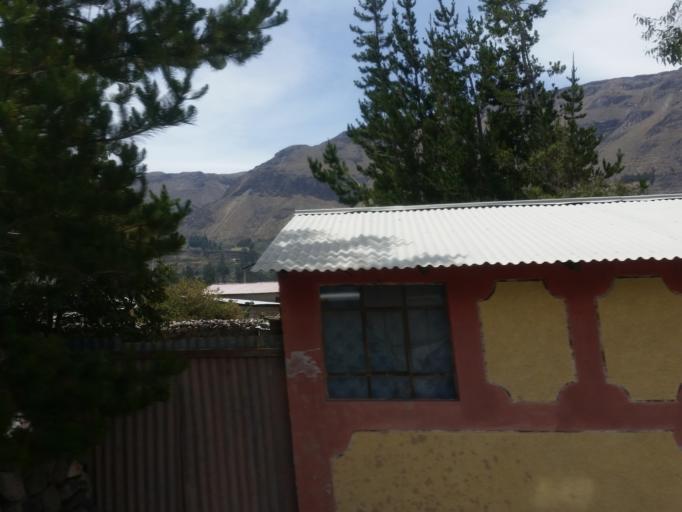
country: PE
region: Arequipa
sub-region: Provincia de Caylloma
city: Maca
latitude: -15.6397
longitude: -71.7678
